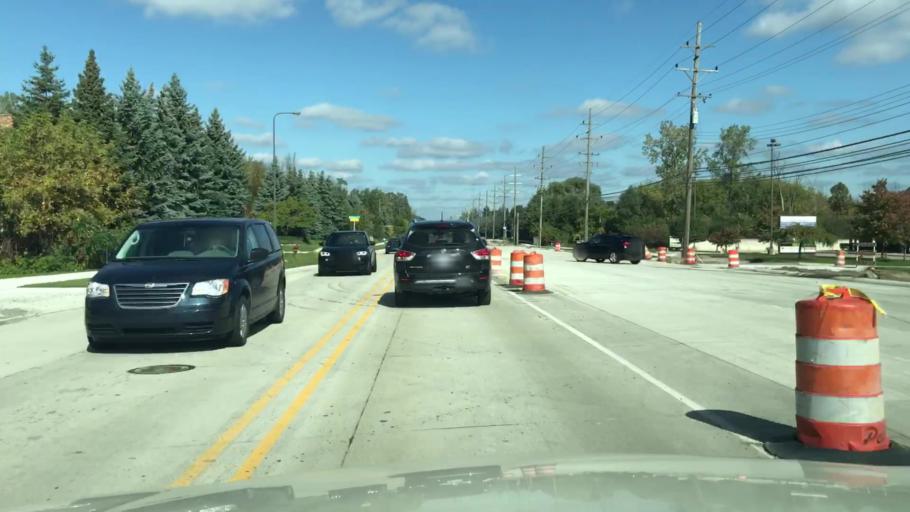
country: US
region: Michigan
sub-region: Oakland County
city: Troy
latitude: 42.6082
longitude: -83.0907
